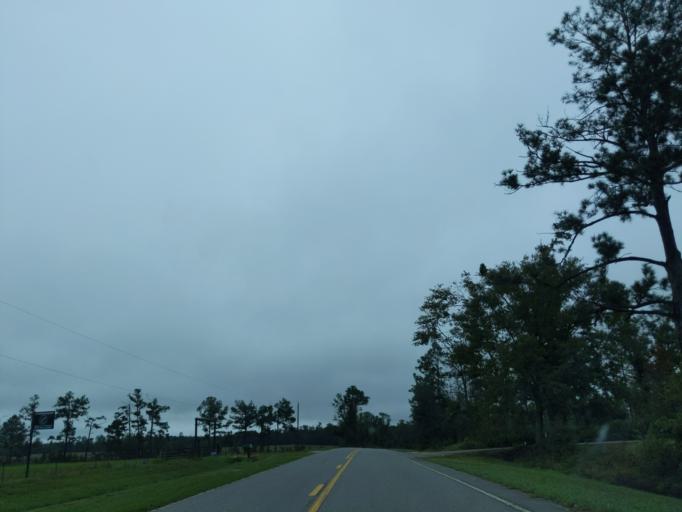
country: US
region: Florida
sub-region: Jackson County
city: Sneads
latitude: 30.6587
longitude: -84.9355
